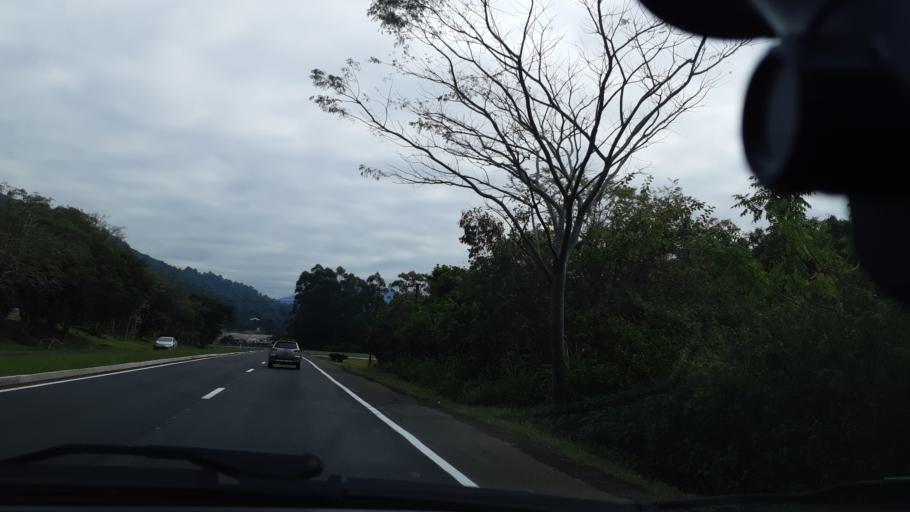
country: BR
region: Rio Grande do Sul
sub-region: Farroupilha
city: Farroupilha
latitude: -29.4035
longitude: -51.3544
